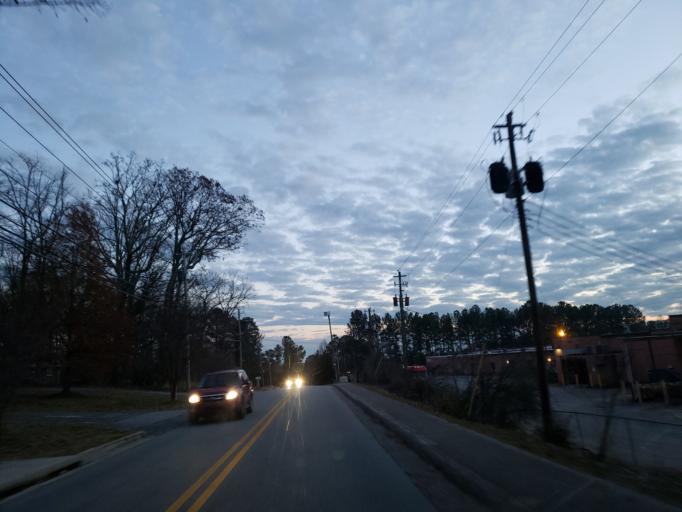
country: US
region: Georgia
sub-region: Cobb County
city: Smyrna
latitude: 33.8623
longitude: -84.5169
